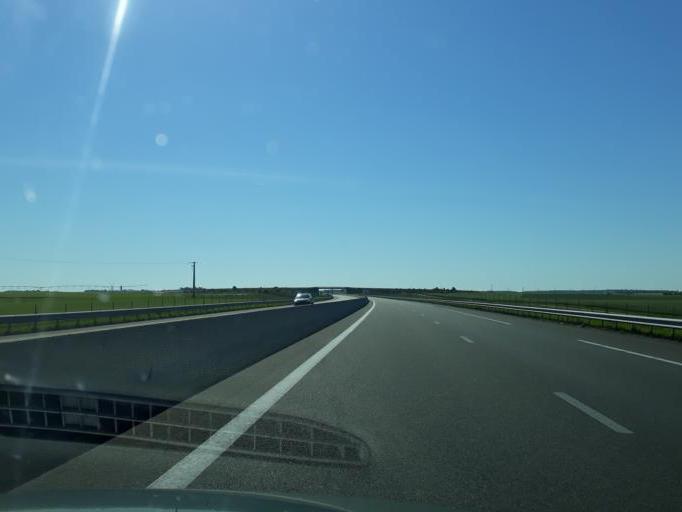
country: FR
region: Centre
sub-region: Departement du Loiret
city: Corbeilles
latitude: 48.0809
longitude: 2.6115
